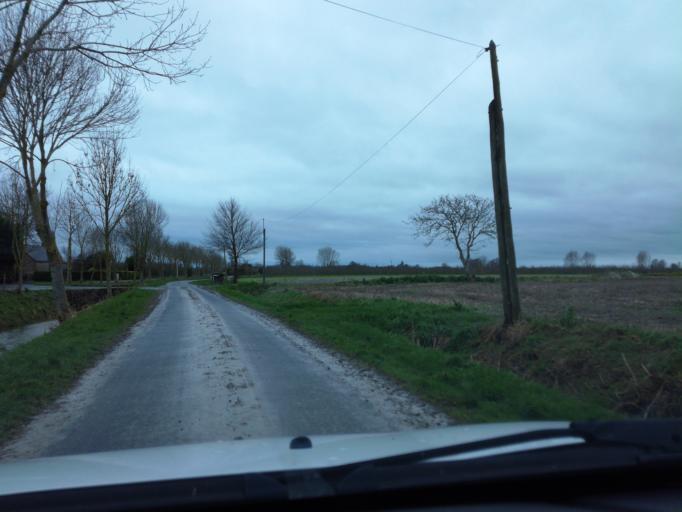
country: FR
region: Brittany
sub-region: Departement d'Ille-et-Vilaine
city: Dol-de-Bretagne
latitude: 48.5660
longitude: -1.7301
